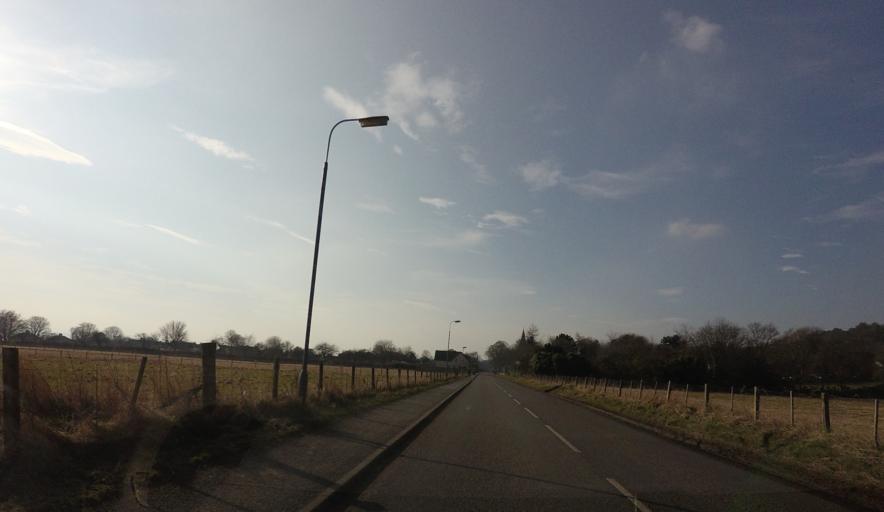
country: GB
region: Scotland
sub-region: Highland
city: Fortrose
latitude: 57.5847
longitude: -4.1249
